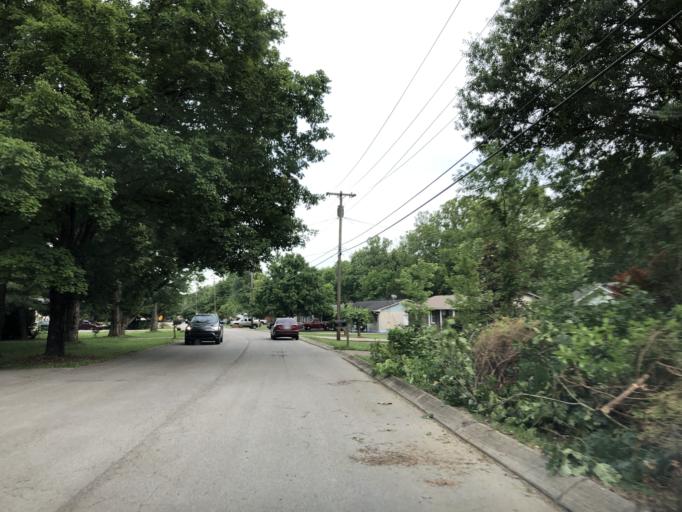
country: US
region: Tennessee
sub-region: Davidson County
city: Goodlettsville
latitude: 36.2893
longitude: -86.7169
